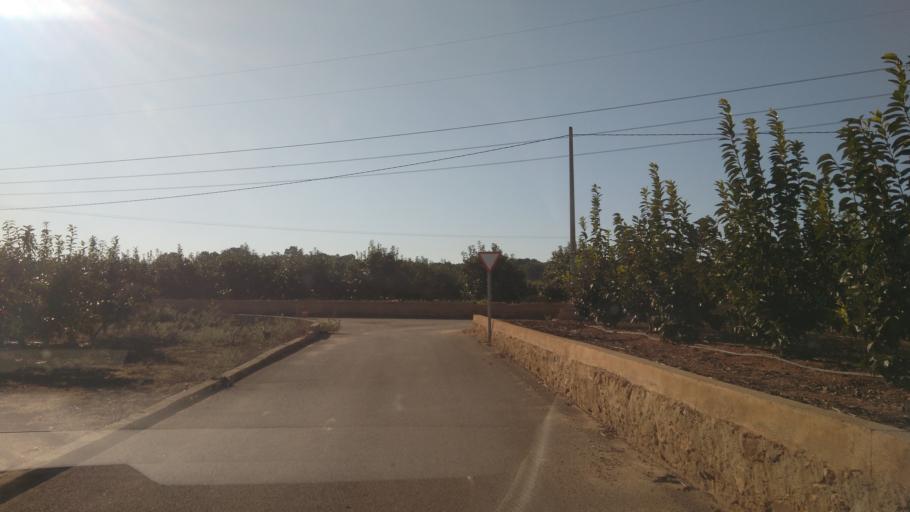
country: ES
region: Valencia
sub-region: Provincia de Valencia
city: Masalaves
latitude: 39.1756
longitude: -0.5516
